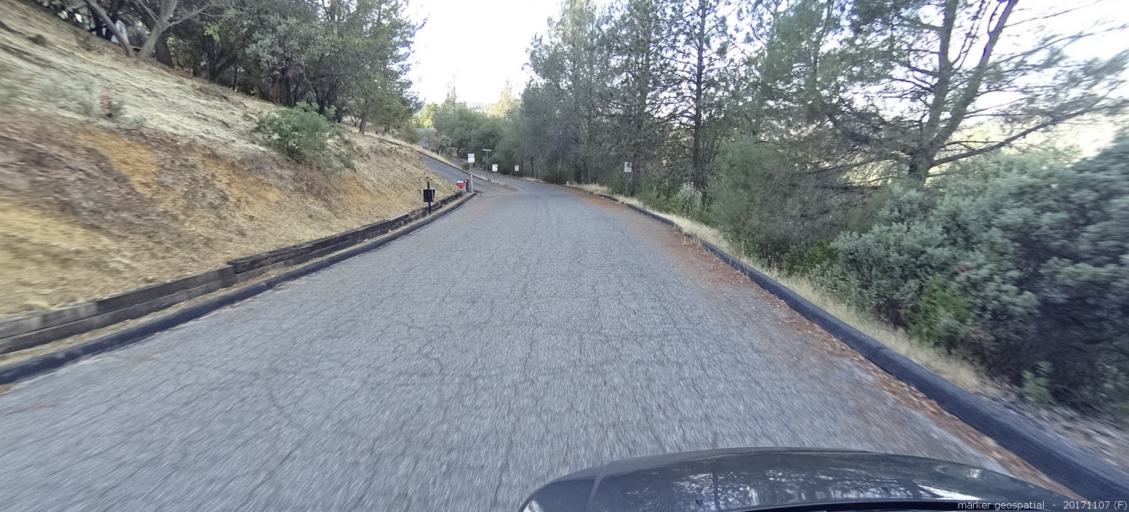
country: US
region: California
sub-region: Shasta County
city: Shasta
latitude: 40.5880
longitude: -122.4734
